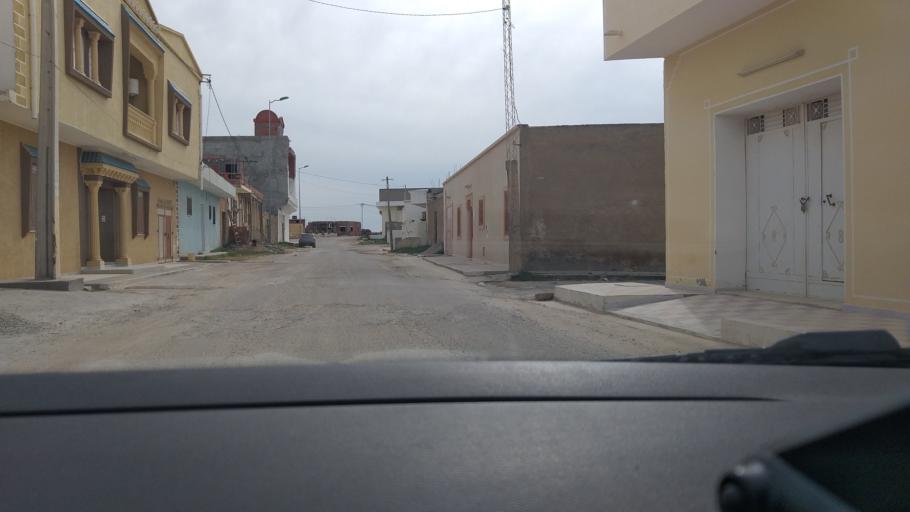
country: TN
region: Al Mahdiyah
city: El Jem
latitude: 35.2845
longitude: 10.7118
